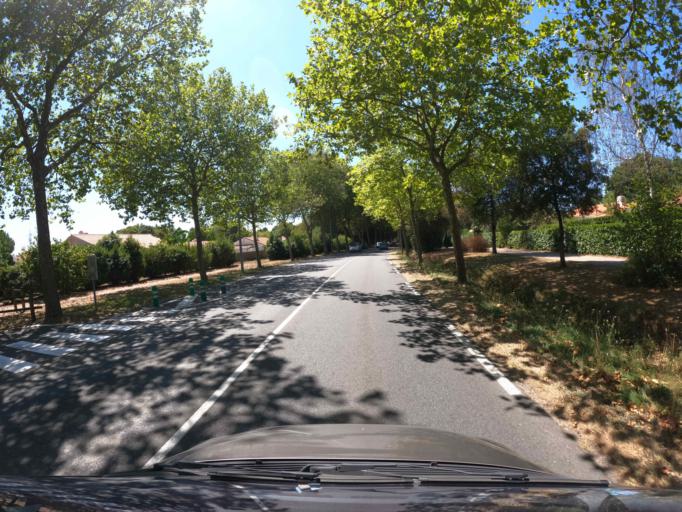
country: FR
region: Pays de la Loire
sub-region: Departement de la Vendee
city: Challans
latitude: 46.8370
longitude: -1.8674
